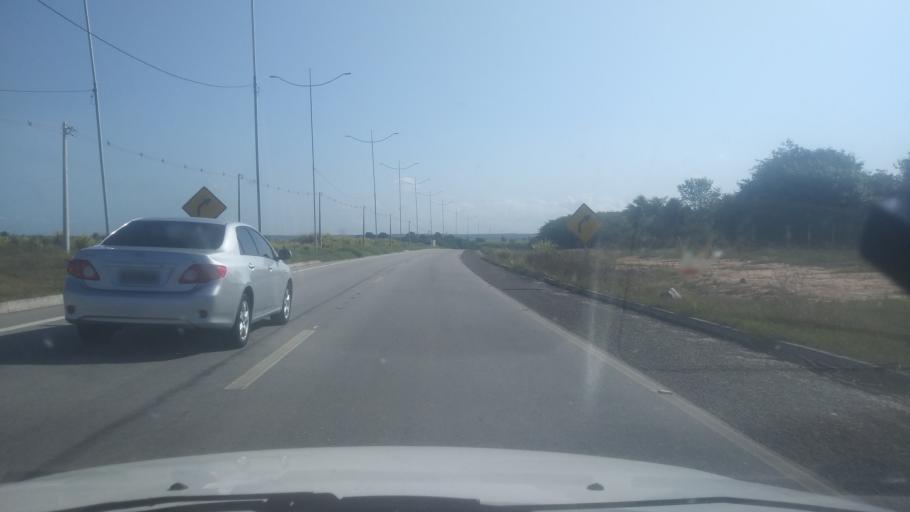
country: BR
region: Rio Grande do Norte
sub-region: Macaiba
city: Macaiba
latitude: -5.8394
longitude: -35.3753
